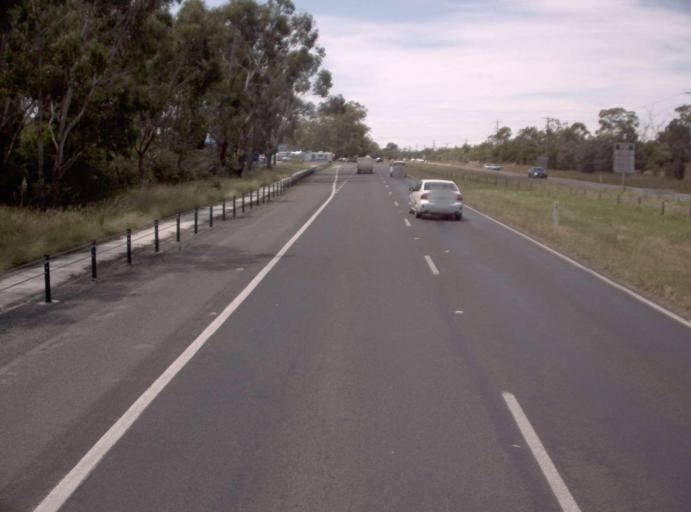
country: AU
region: Victoria
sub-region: Latrobe
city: Traralgon
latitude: -38.2172
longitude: 146.4768
